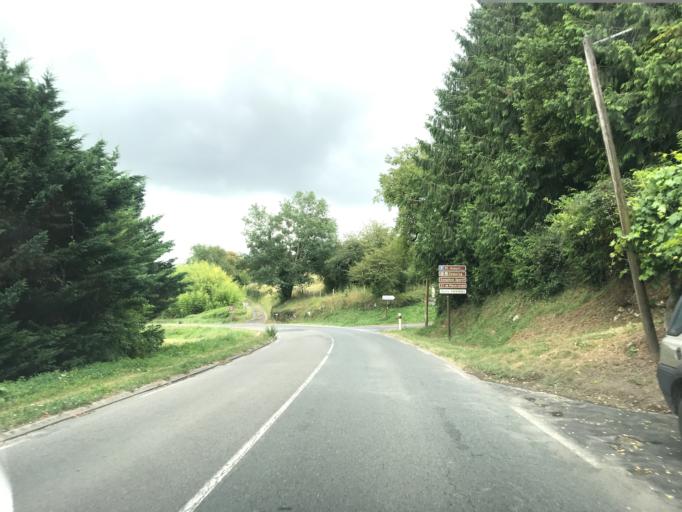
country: FR
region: Aquitaine
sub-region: Departement de la Dordogne
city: Brantome
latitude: 45.3706
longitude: 0.6452
